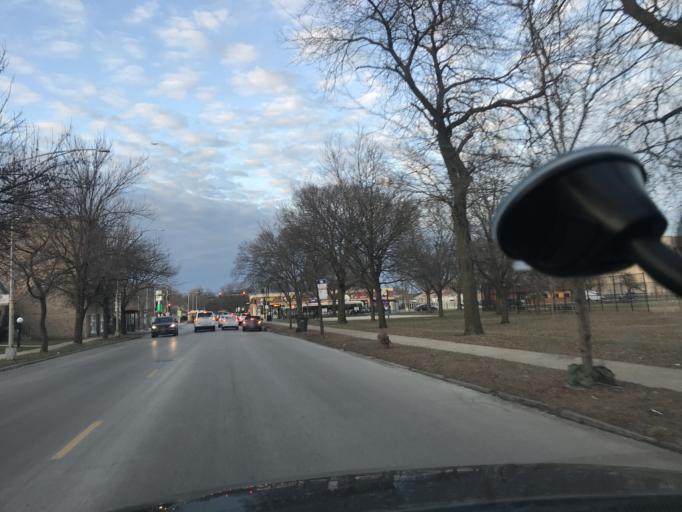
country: US
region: Indiana
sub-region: Lake County
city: Whiting
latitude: 41.7360
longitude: -87.5757
